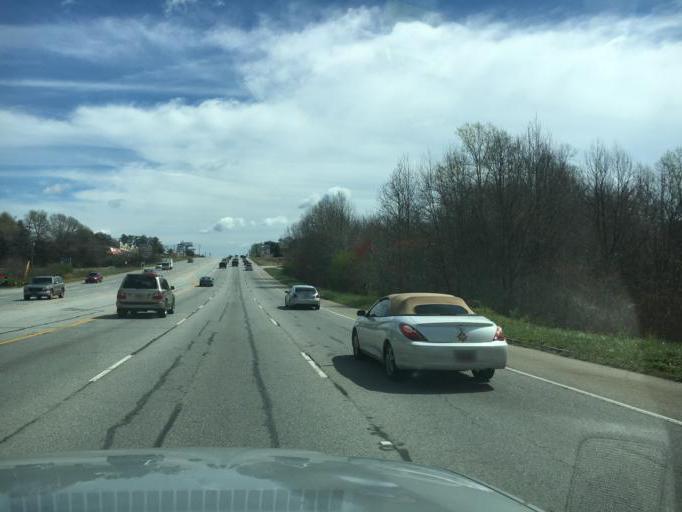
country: US
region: South Carolina
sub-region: Greenville County
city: Taylors
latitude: 34.9308
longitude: -82.2908
